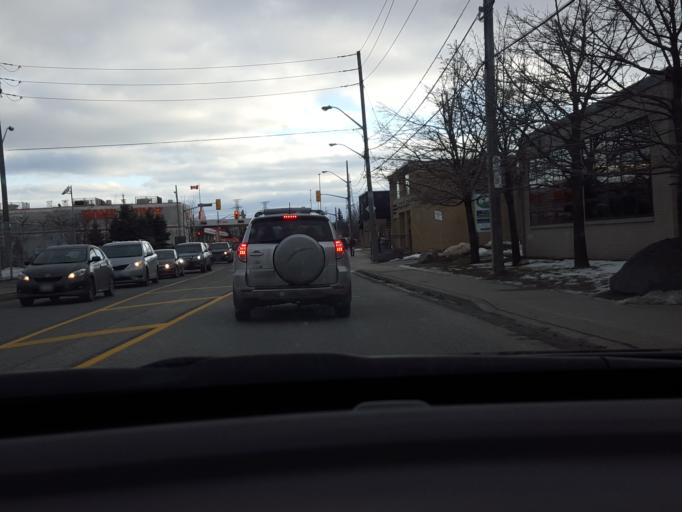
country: CA
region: Ontario
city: Toronto
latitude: 43.7126
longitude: -79.3590
